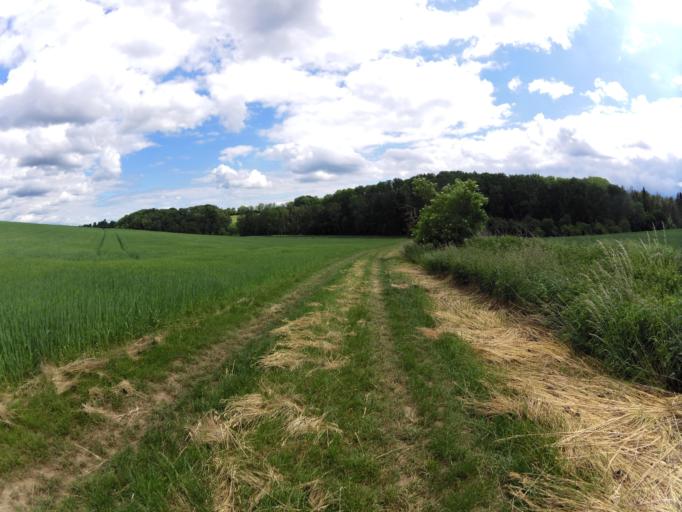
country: DE
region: Bavaria
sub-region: Regierungsbezirk Unterfranken
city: Gaukonigshofen
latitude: 49.6690
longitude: 9.9934
